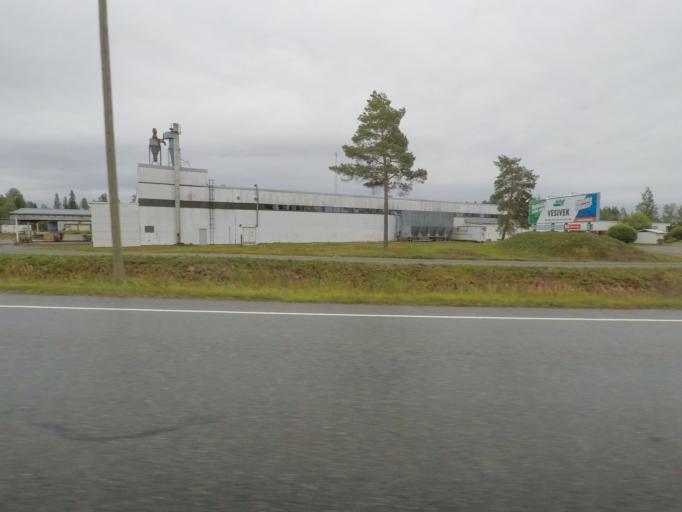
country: FI
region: Southern Savonia
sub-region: Pieksaemaeki
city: Juva
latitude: 61.9012
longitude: 27.8039
